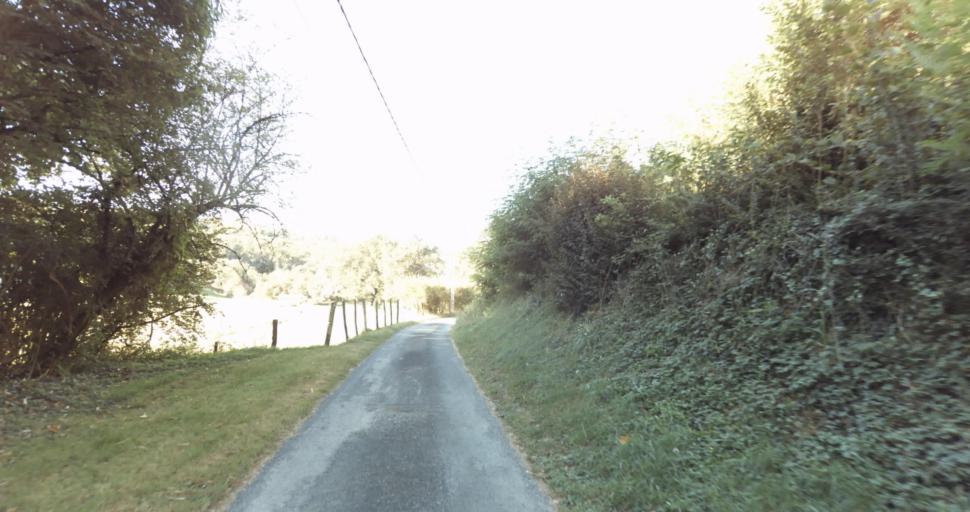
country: FR
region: Rhone-Alpes
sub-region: Departement du Rhone
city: Montanay
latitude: 45.8909
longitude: 4.8650
